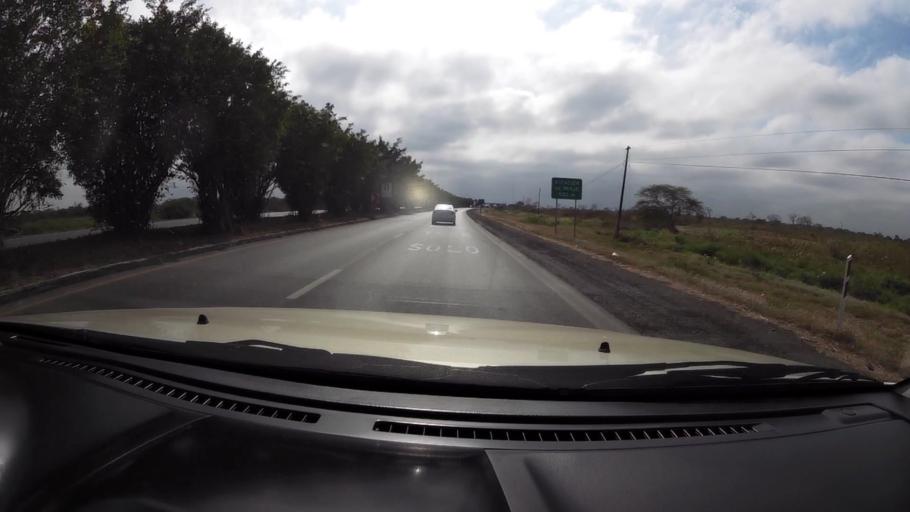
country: EC
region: Guayas
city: Eloy Alfaro
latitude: -2.2003
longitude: -79.7589
